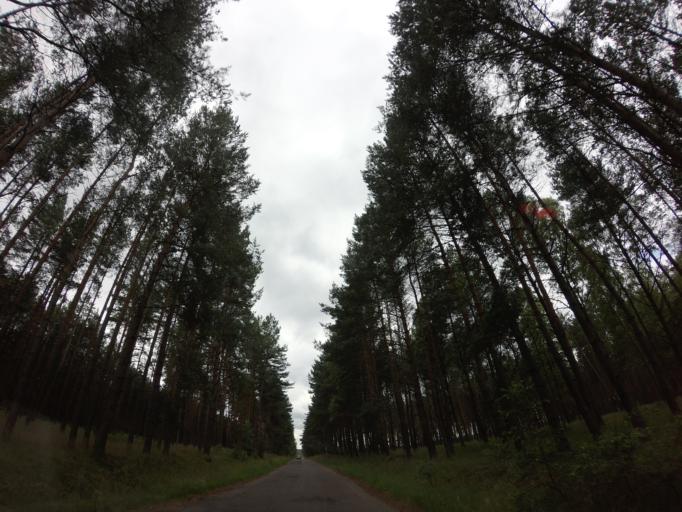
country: PL
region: West Pomeranian Voivodeship
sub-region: Powiat stargardzki
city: Insko
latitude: 53.4163
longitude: 15.6023
